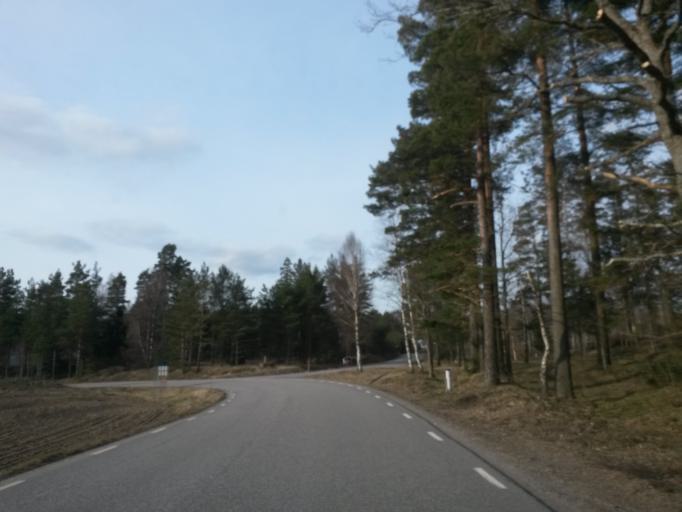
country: SE
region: Vaestra Goetaland
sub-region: Vargarda Kommun
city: Jonstorp
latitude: 57.9881
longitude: 12.7698
